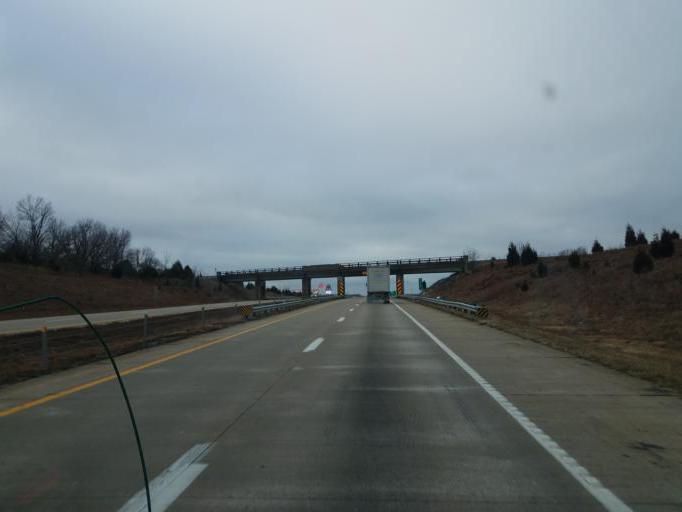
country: US
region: Missouri
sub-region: Laclede County
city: Lebanon
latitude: 37.5632
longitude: -92.7820
